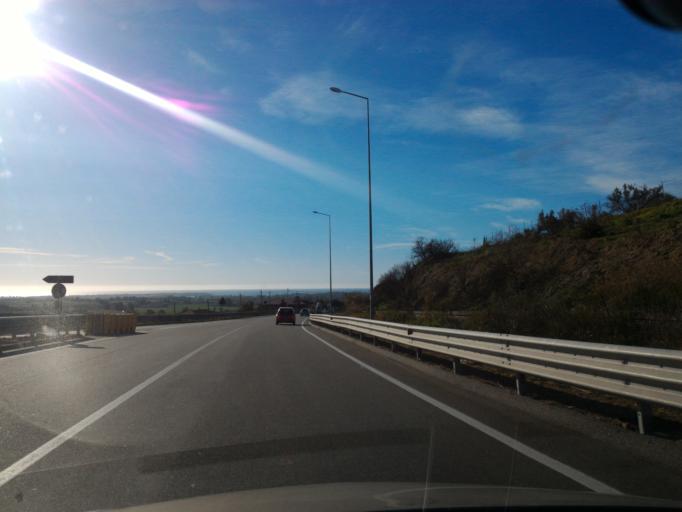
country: IT
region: Calabria
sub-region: Provincia di Crotone
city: Isola di Capo Rizzuto
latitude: 38.9494
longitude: 17.0827
